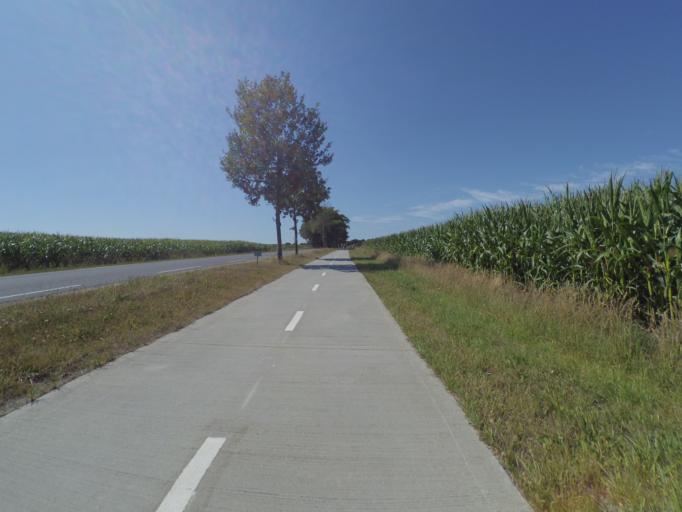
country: NL
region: Drenthe
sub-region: Gemeente Assen
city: Assen
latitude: 52.8902
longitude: 6.6542
